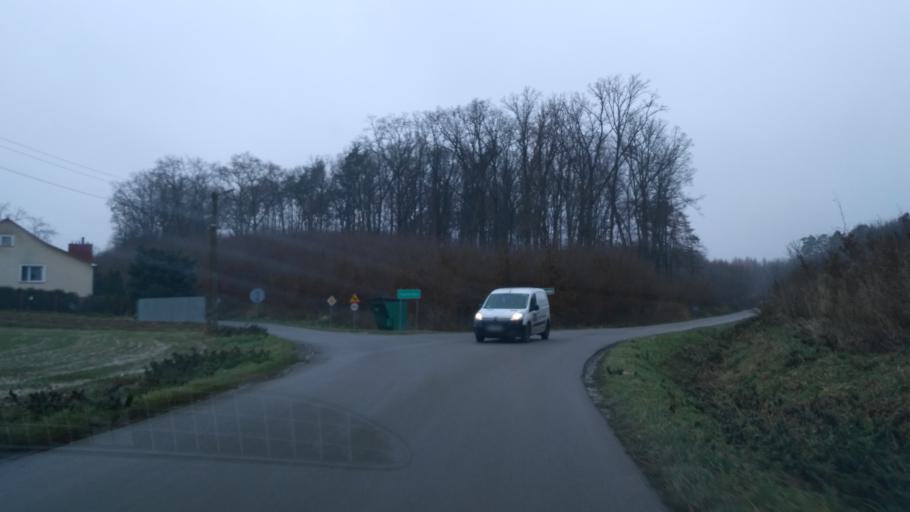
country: PL
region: Subcarpathian Voivodeship
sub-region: Powiat przeworski
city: Zarzecze
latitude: 49.9951
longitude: 22.5172
